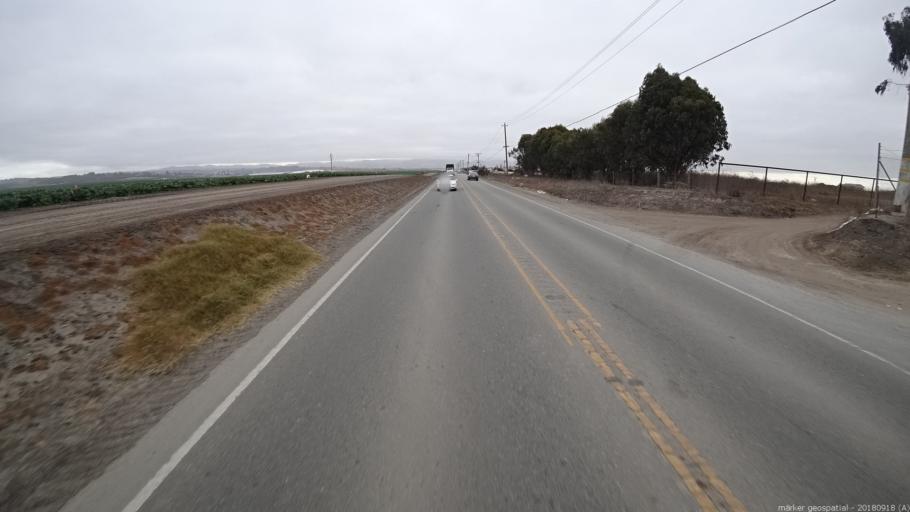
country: US
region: California
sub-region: Monterey County
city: Castroville
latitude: 36.7480
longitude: -121.7122
